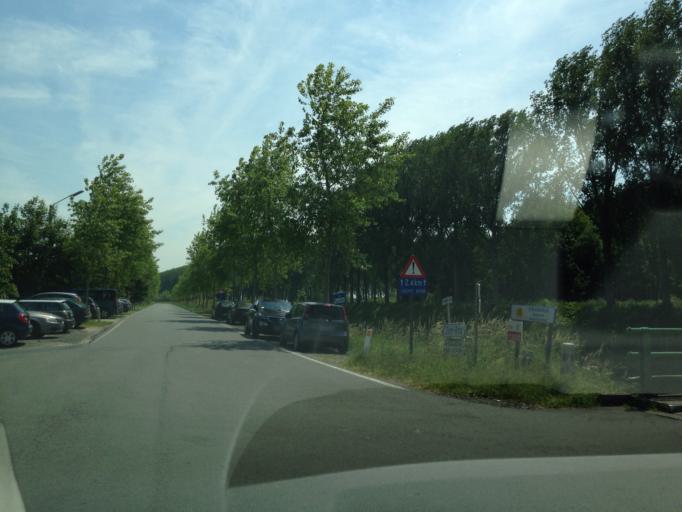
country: BE
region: Flanders
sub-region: Provincie West-Vlaanderen
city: Damme
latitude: 51.2664
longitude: 3.2978
